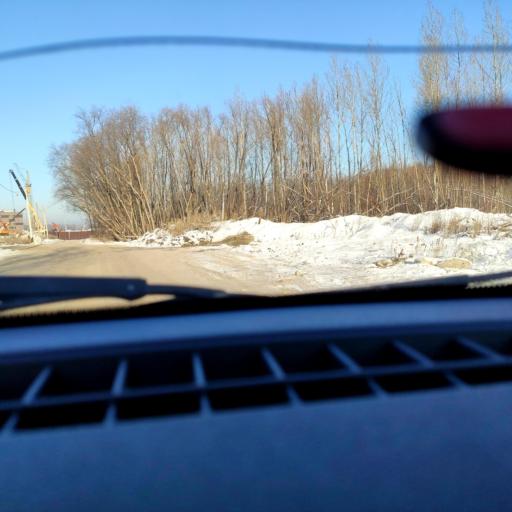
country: RU
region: Bashkortostan
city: Ufa
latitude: 54.6695
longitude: 55.9216
